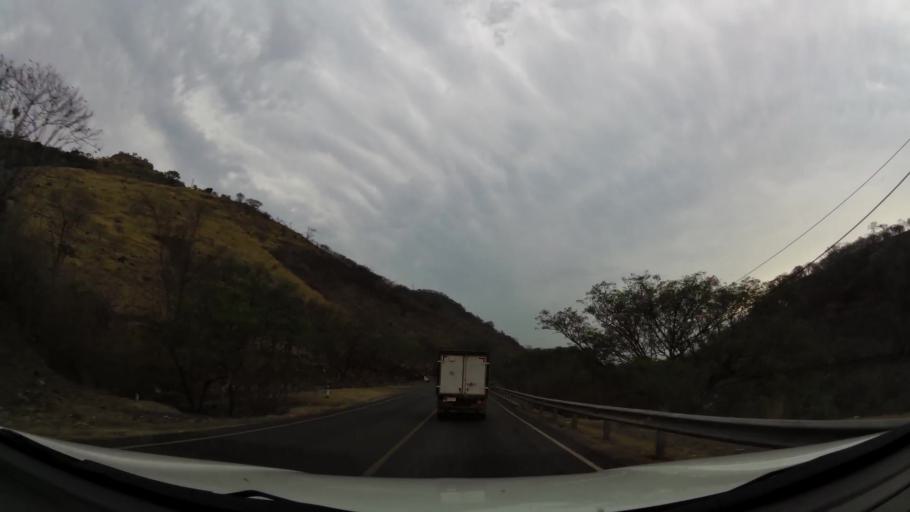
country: NI
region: Esteli
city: Esteli
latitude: 12.9443
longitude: -86.2193
